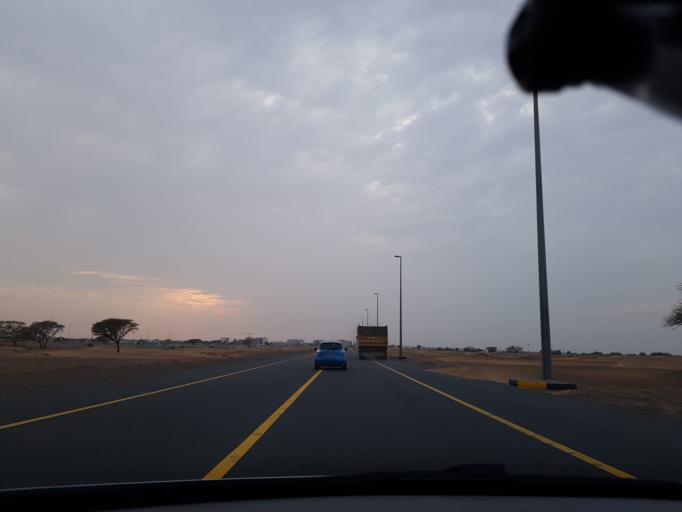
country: AE
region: Ash Shariqah
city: Adh Dhayd
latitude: 25.2692
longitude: 55.9045
